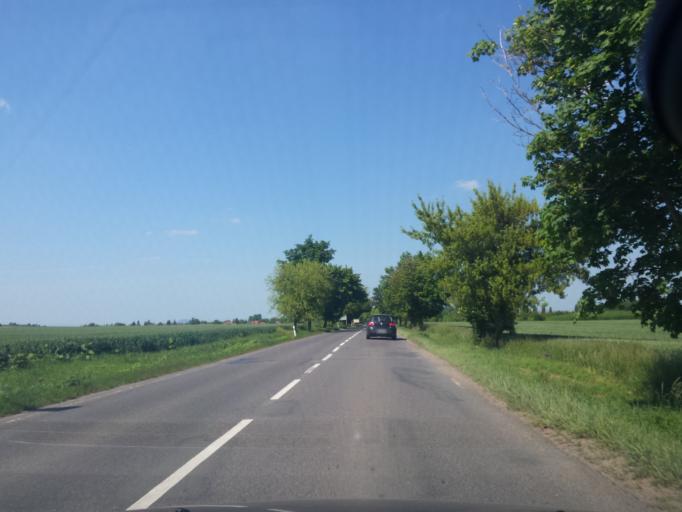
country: CZ
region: Central Bohemia
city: Velke Prilepy
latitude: 50.1793
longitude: 14.3197
